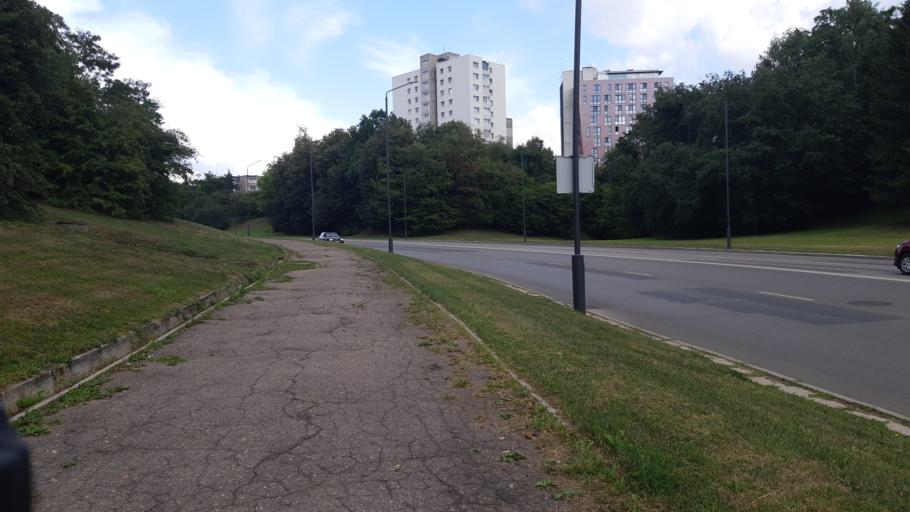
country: LT
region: Kauno apskritis
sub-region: Kaunas
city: Eiguliai
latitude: 54.9276
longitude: 23.9222
